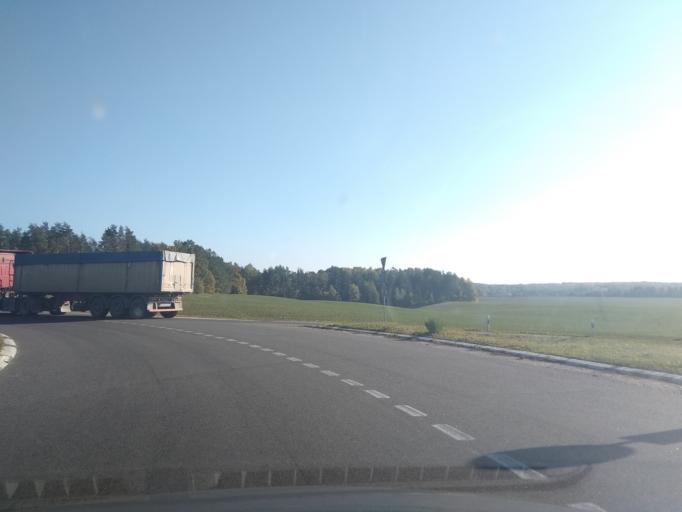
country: BY
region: Grodnenskaya
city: Slonim
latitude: 53.0576
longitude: 25.3018
